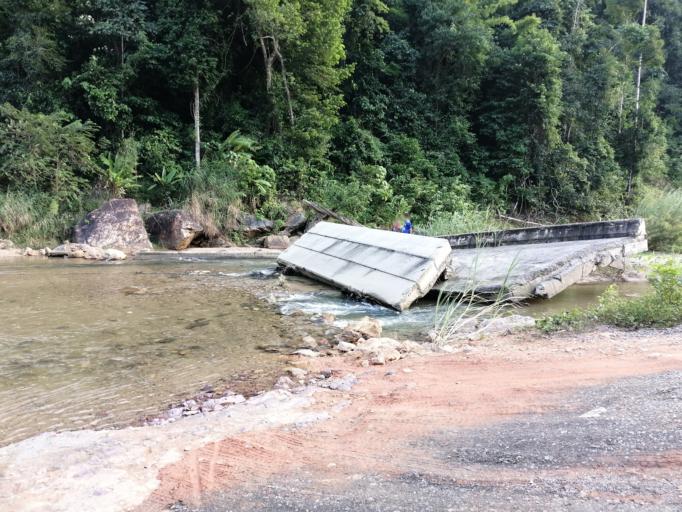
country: TH
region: Nakhon Si Thammarat
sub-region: Amphoe Nopphitam
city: Nopphitam
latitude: 8.9259
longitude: 99.6400
